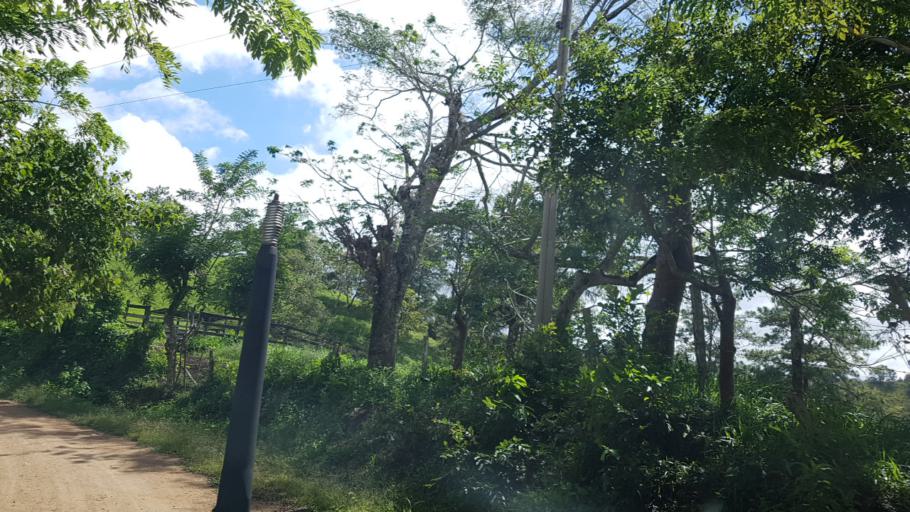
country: NI
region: Nueva Segovia
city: Ciudad Antigua
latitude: 13.6517
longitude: -86.2421
